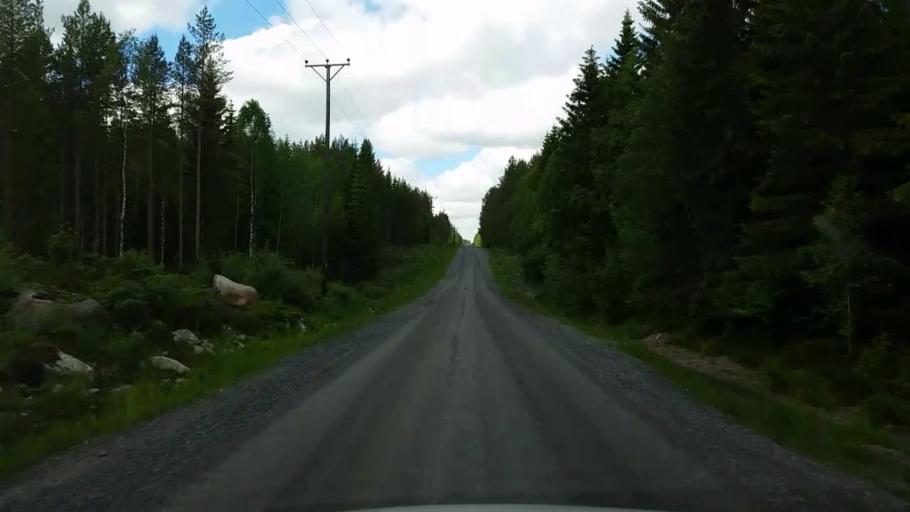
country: SE
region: Gaevleborg
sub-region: Bollnas Kommun
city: Vittsjo
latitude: 61.0693
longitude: 16.2809
